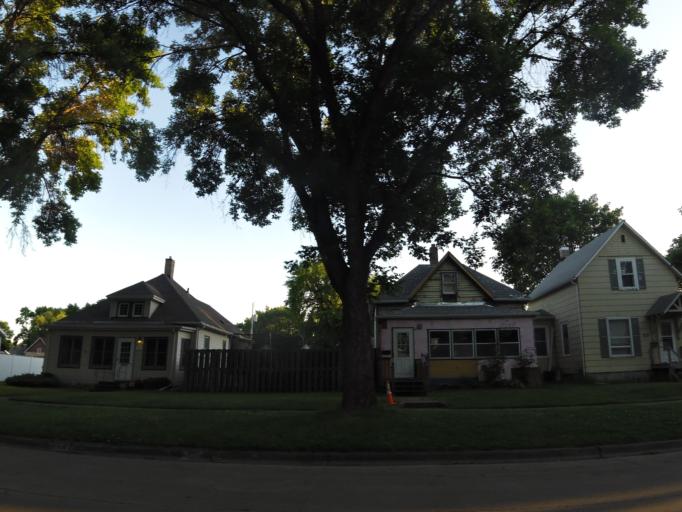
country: US
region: North Dakota
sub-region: Grand Forks County
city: Grand Forks
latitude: 47.9299
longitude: -97.0411
